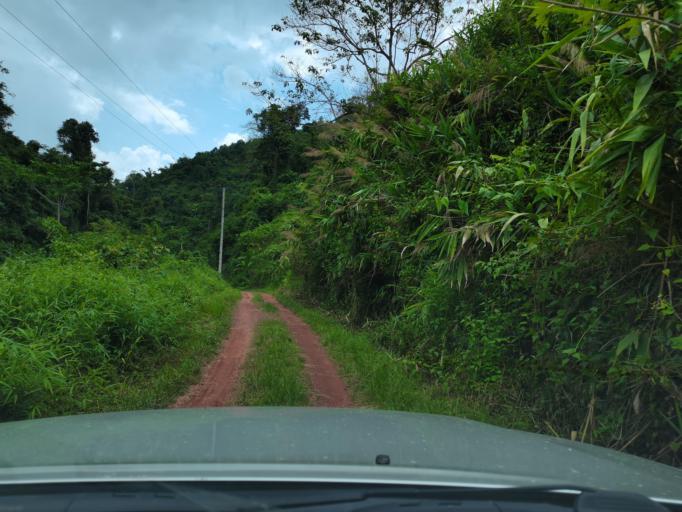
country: LA
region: Loungnamtha
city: Muang Nale
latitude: 20.5147
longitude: 101.0773
